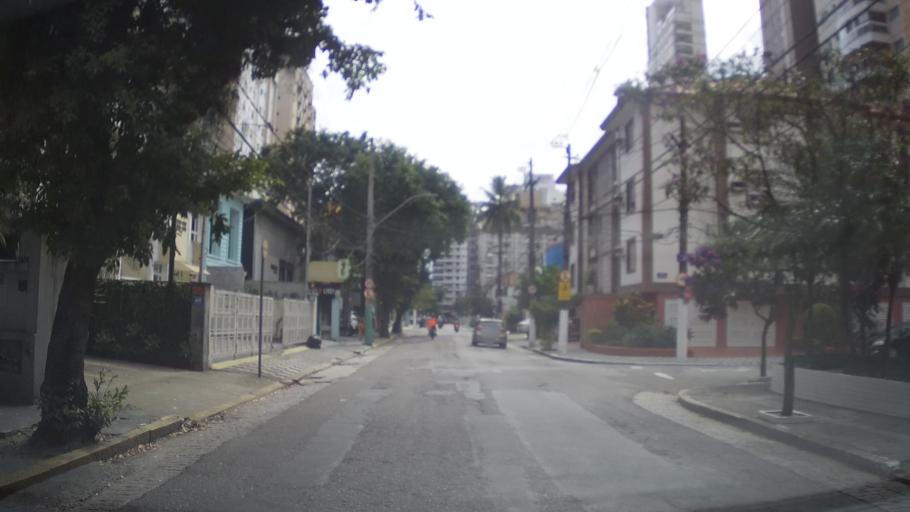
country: BR
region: Sao Paulo
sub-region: Santos
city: Santos
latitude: -23.9664
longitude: -46.3255
